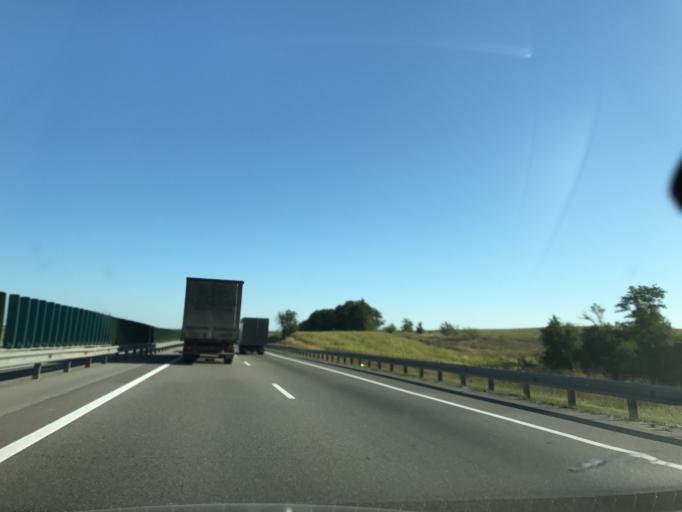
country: RU
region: Rostov
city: Tarasovskiy
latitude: 48.7689
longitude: 40.3786
